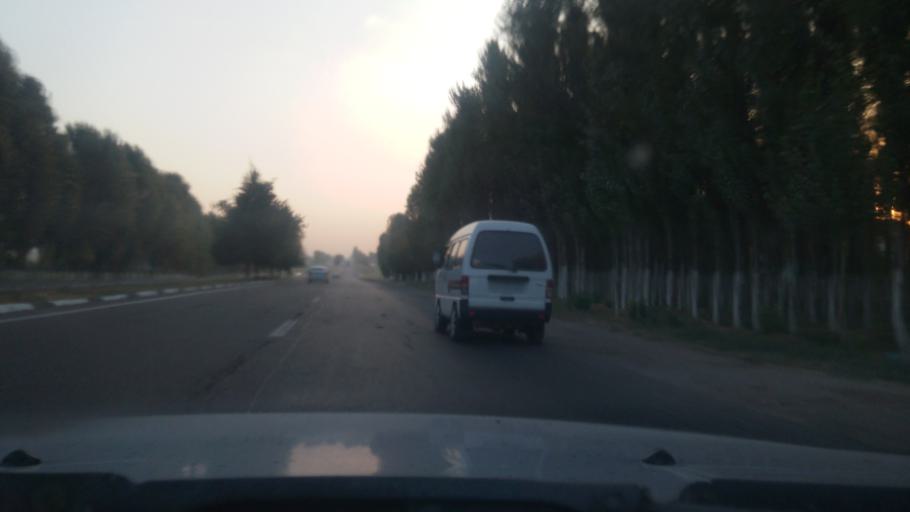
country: UZ
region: Toshkent
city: Amir Timur
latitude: 41.0868
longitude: 68.9471
